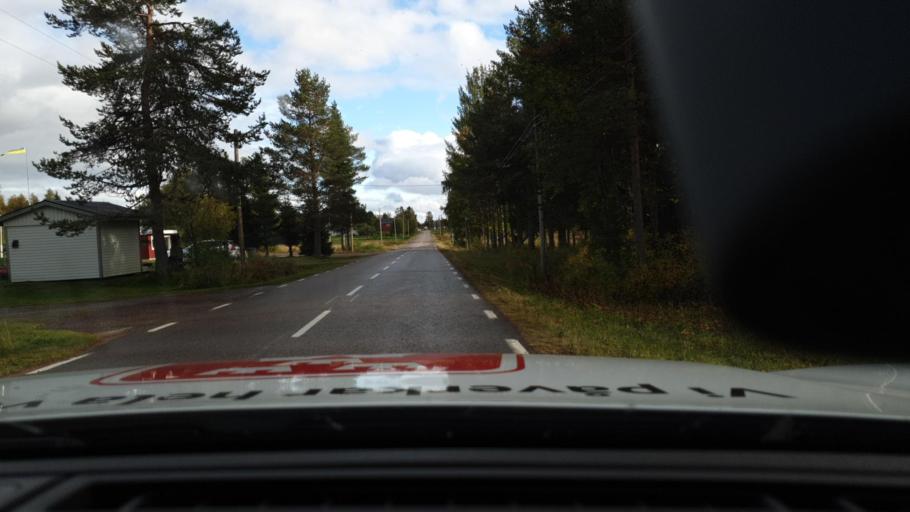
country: SE
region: Norrbotten
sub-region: Overkalix Kommun
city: OEverkalix
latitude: 67.0071
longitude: 22.4874
